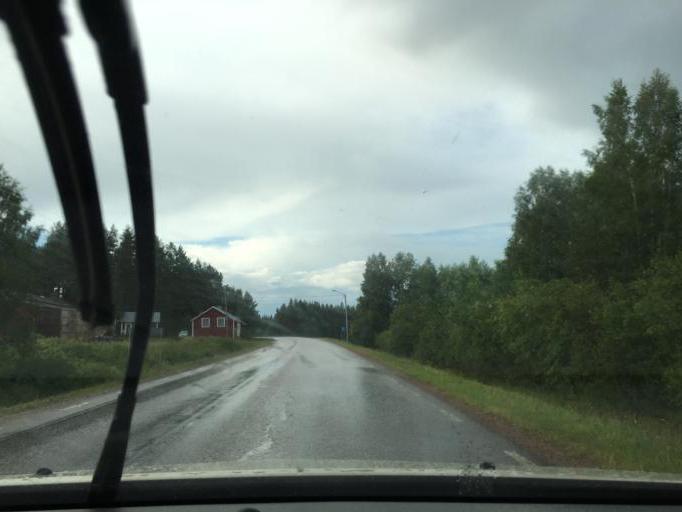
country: SE
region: Norrbotten
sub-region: Kalix Kommun
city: Toere
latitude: 65.9471
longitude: 22.8913
